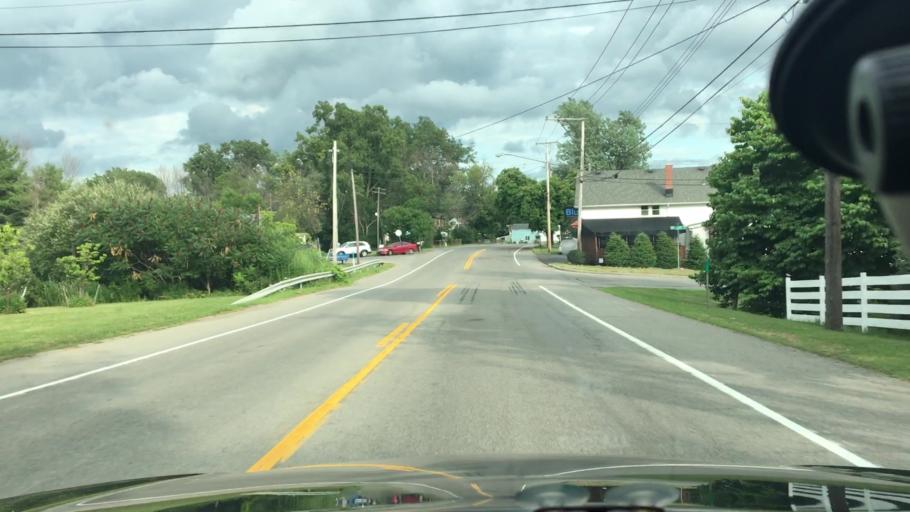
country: US
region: New York
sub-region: Erie County
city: Elma Center
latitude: 42.8228
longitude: -78.6834
